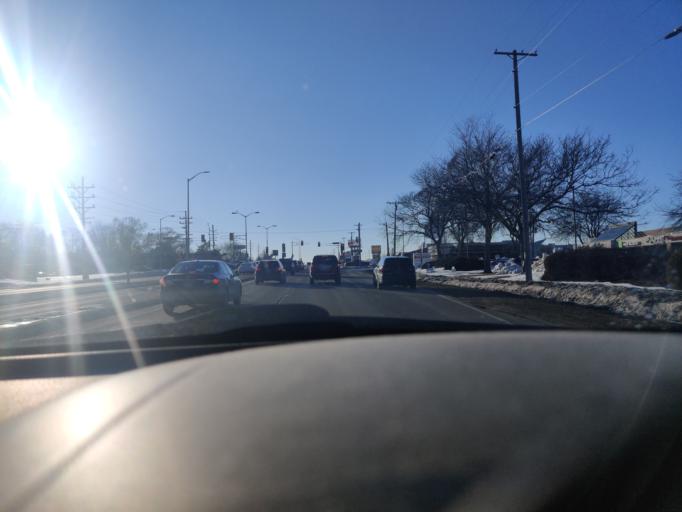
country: US
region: Wisconsin
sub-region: Kenosha County
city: Pleasant Prairie
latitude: 42.5664
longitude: -87.8792
